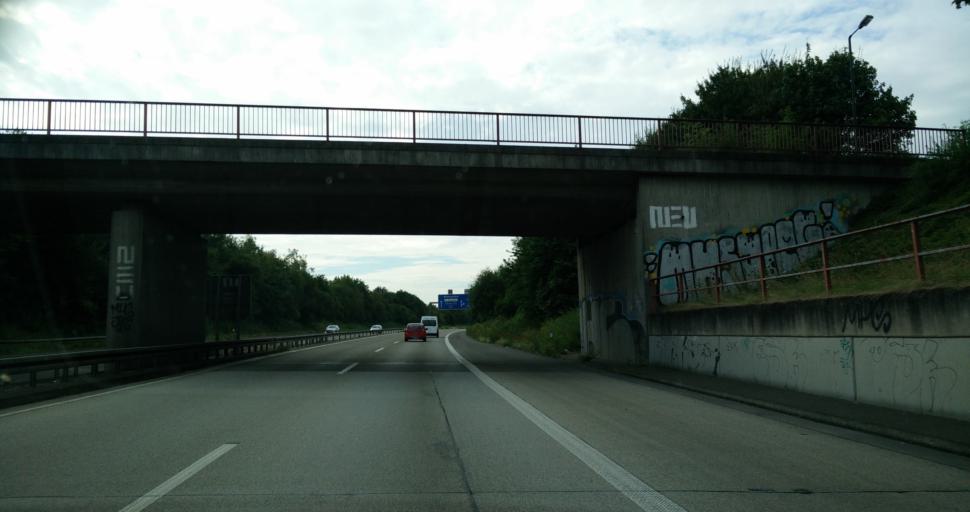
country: DE
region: North Rhine-Westphalia
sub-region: Regierungsbezirk Dusseldorf
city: Ratingen
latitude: 51.2738
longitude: 6.8221
